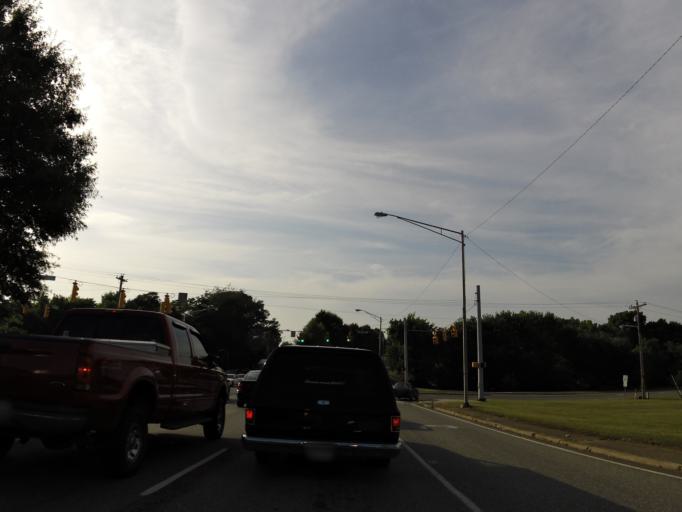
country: US
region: Tennessee
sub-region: Blount County
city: Maryville
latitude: 35.7724
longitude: -83.9776
